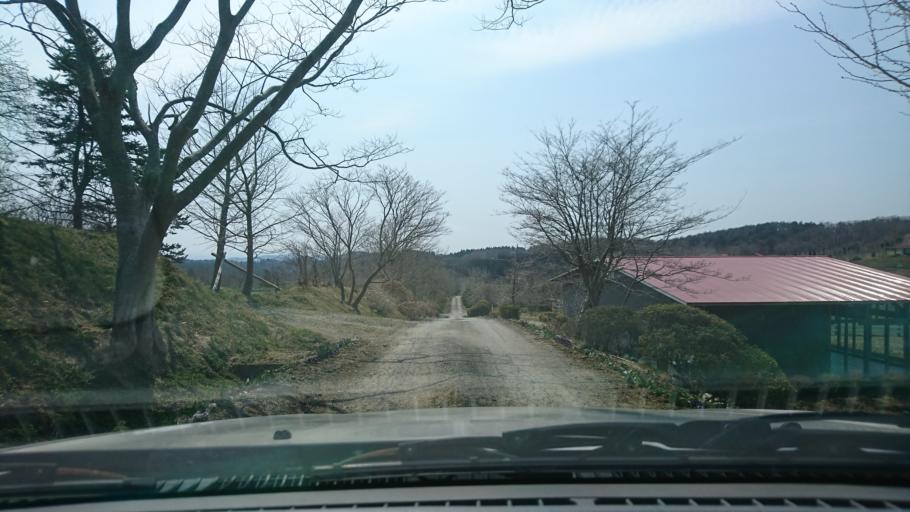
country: JP
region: Iwate
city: Ichinoseki
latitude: 38.8215
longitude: 141.2685
